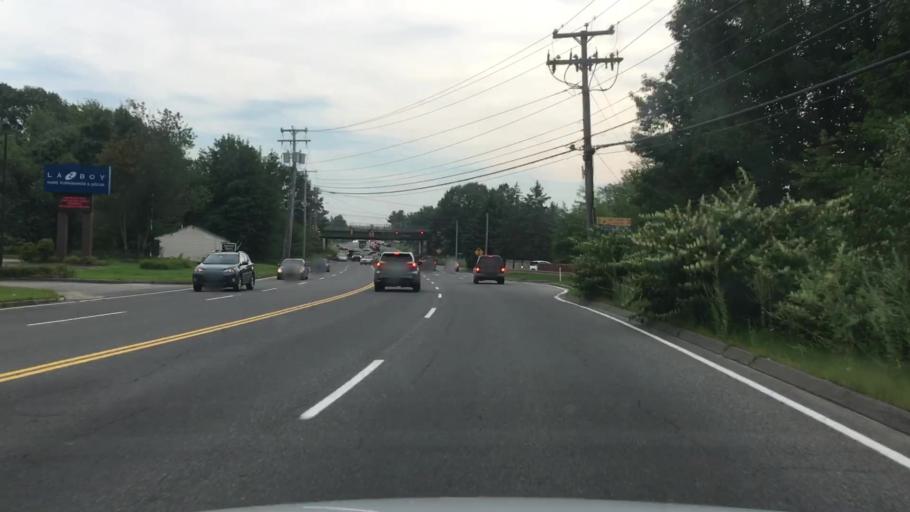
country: US
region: Maine
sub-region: Cumberland County
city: South Portland Gardens
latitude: 43.6276
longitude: -70.3458
